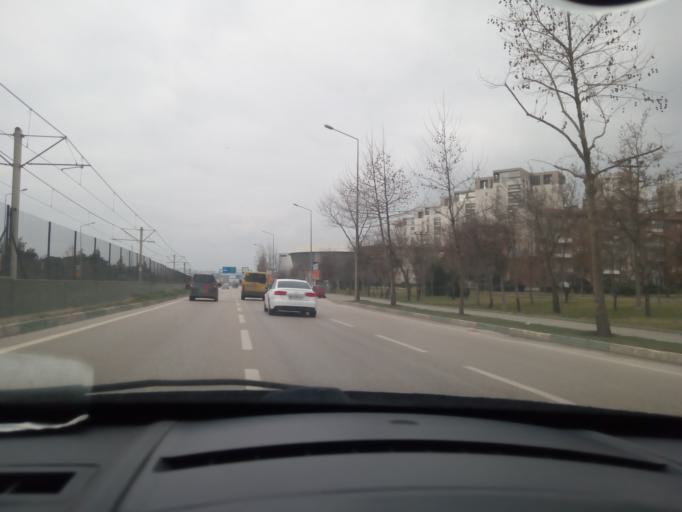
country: TR
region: Bursa
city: Niluefer
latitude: 40.2472
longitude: 28.9622
